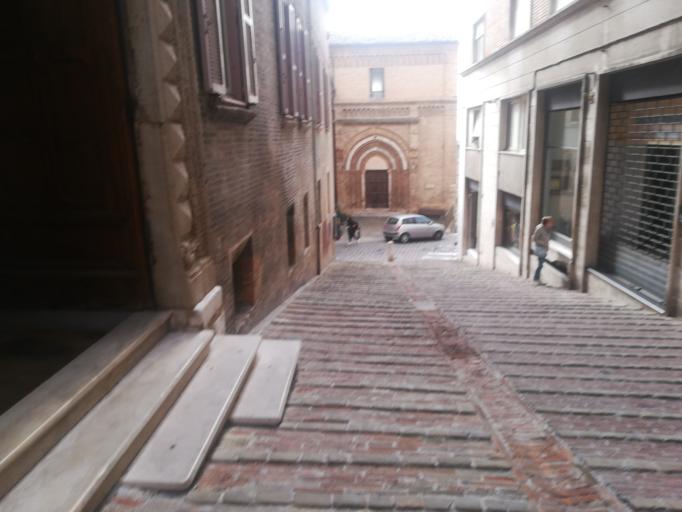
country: IT
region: The Marches
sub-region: Provincia di Macerata
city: Macerata
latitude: 43.2998
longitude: 13.4536
